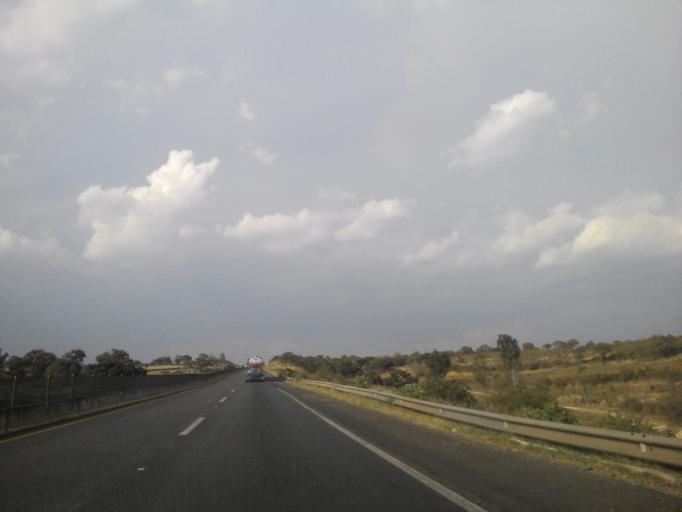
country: MX
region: Jalisco
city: Tepatitlan de Morelos
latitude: 20.8477
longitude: -102.7795
